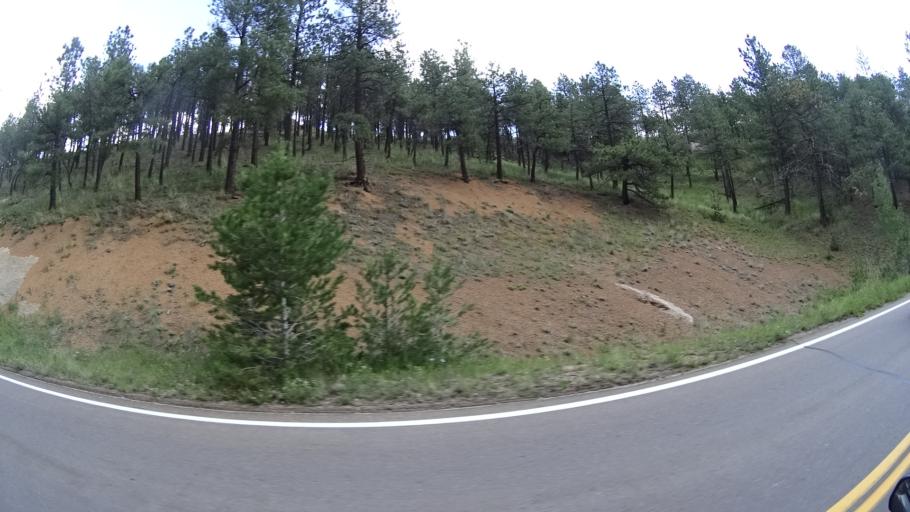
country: US
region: Colorado
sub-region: El Paso County
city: Cascade-Chipita Park
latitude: 38.9115
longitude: -105.0193
